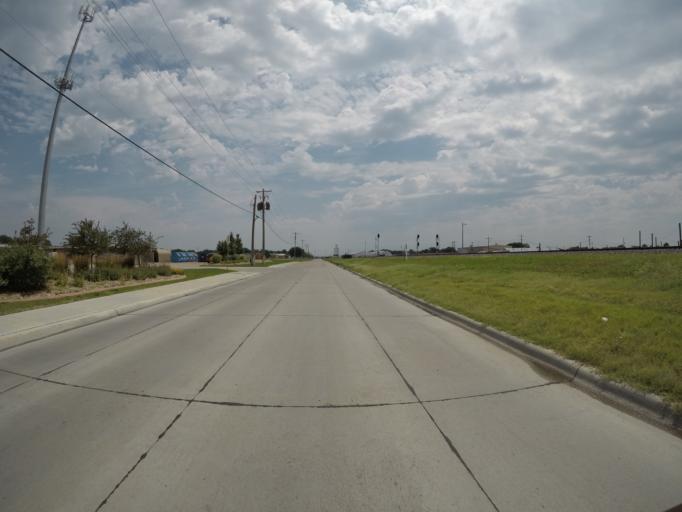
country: US
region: Nebraska
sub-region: Buffalo County
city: Kearney
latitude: 40.6936
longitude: -99.1003
